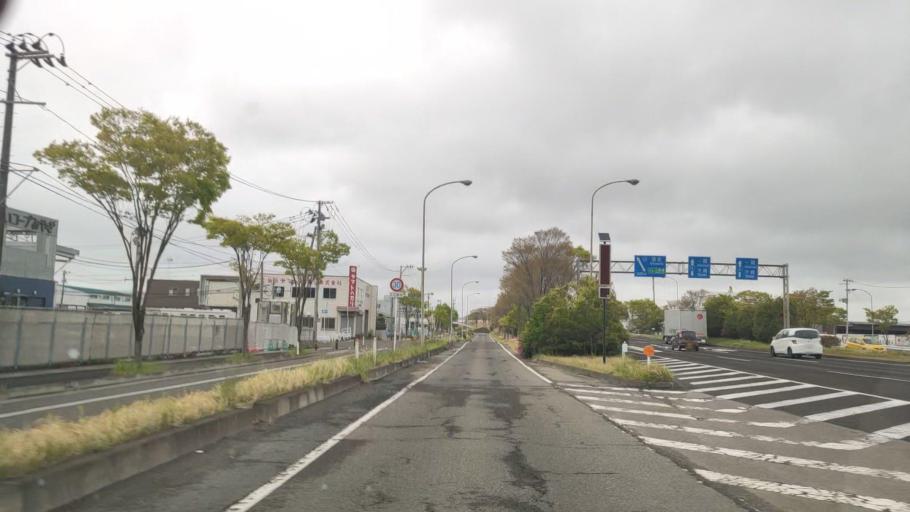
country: JP
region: Miyagi
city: Sendai-shi
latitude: 38.2648
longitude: 140.9380
